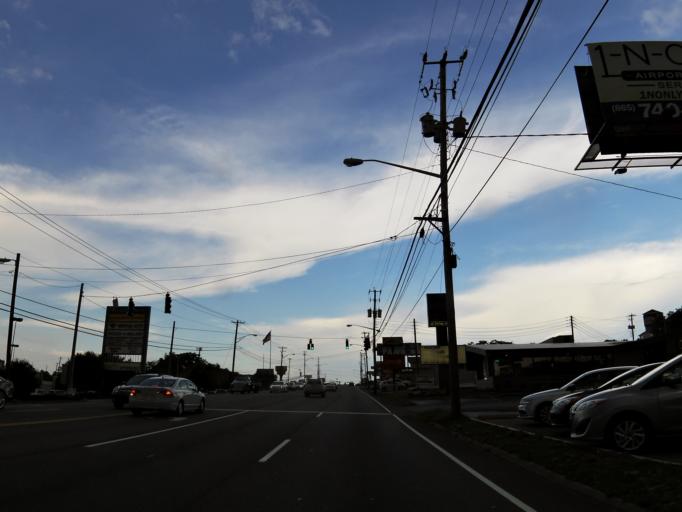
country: US
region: Tennessee
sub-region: Knox County
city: Farragut
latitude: 35.9219
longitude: -84.0629
